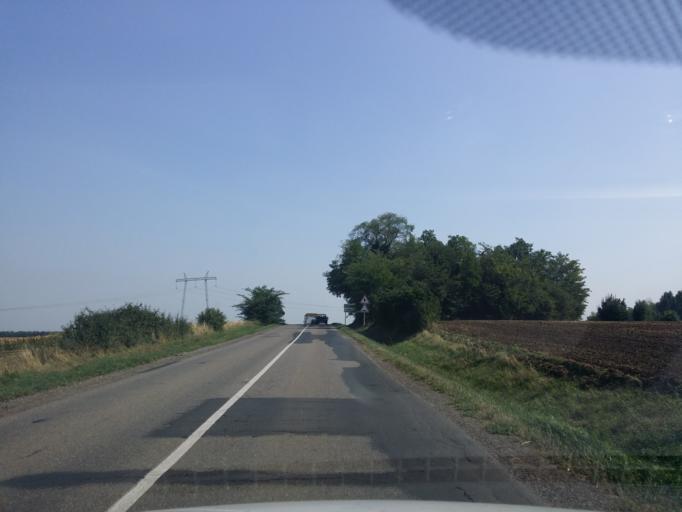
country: HU
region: Fejer
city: Mezofalva
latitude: 46.9453
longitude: 18.7434
